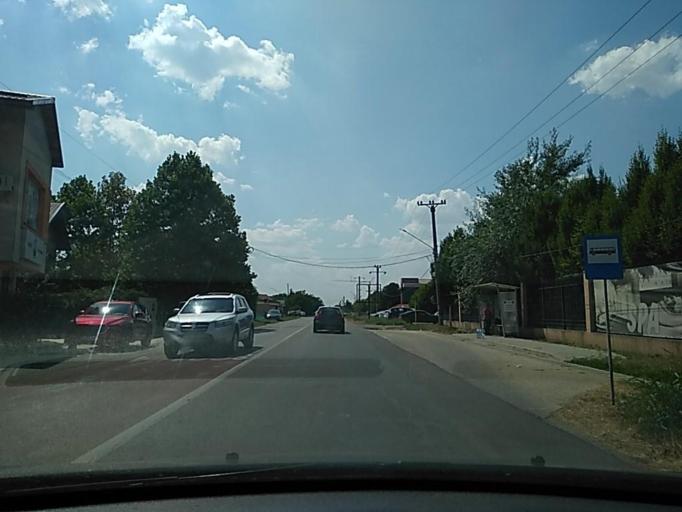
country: RO
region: Ilfov
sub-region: Comuna Clinceni
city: Olteni
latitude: 44.4033
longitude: 25.9535
